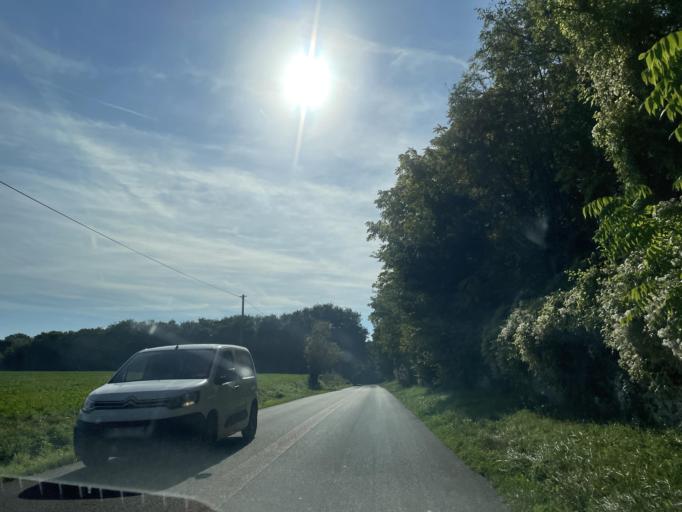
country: FR
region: Ile-de-France
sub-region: Departement de Seine-et-Marne
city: Saint-Jean-les-Deux-Jumeaux
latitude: 48.9388
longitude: 2.9861
